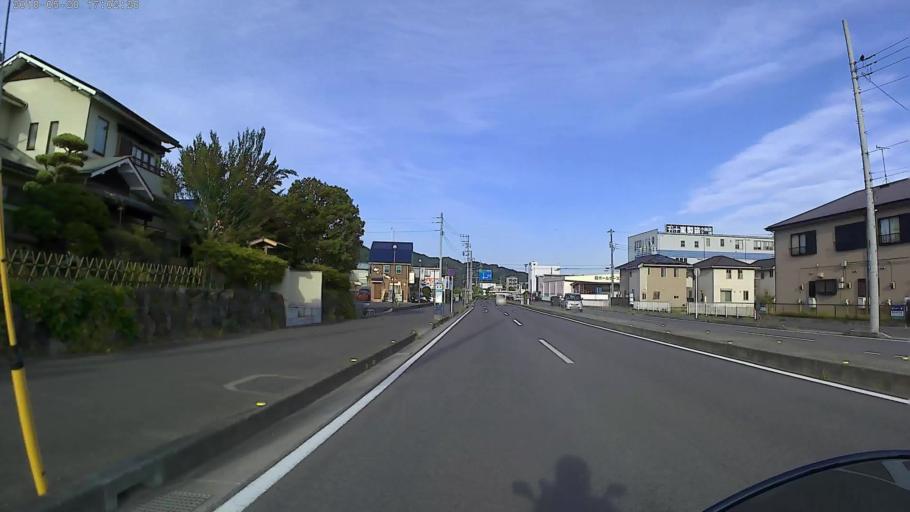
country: JP
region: Kanagawa
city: Odawara
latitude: 35.2896
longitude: 139.1872
